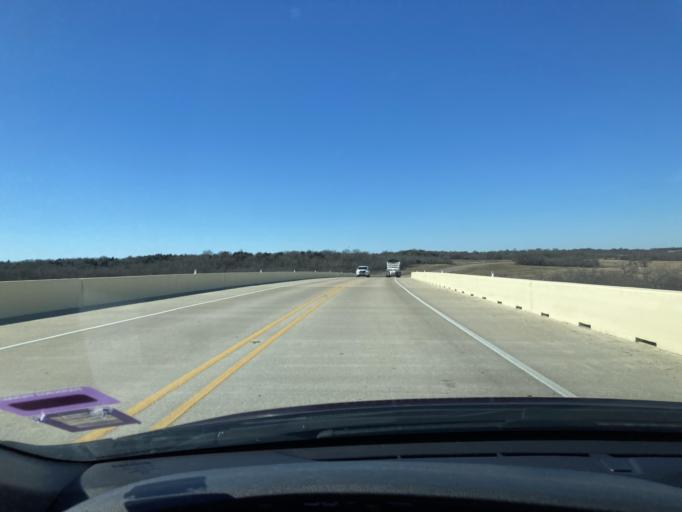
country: US
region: Texas
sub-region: Navarro County
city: Corsicana
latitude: 32.0409
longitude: -96.4536
